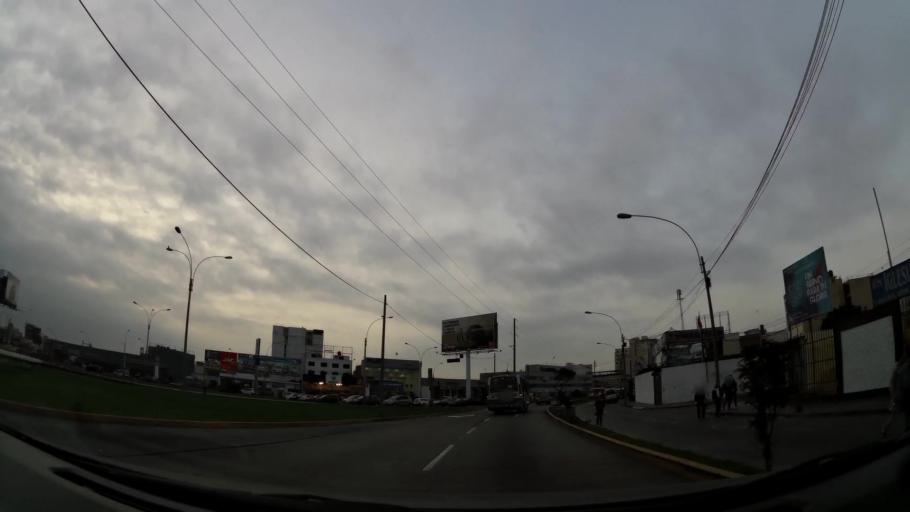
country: PE
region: Callao
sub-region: Callao
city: Callao
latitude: -12.0738
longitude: -77.0992
